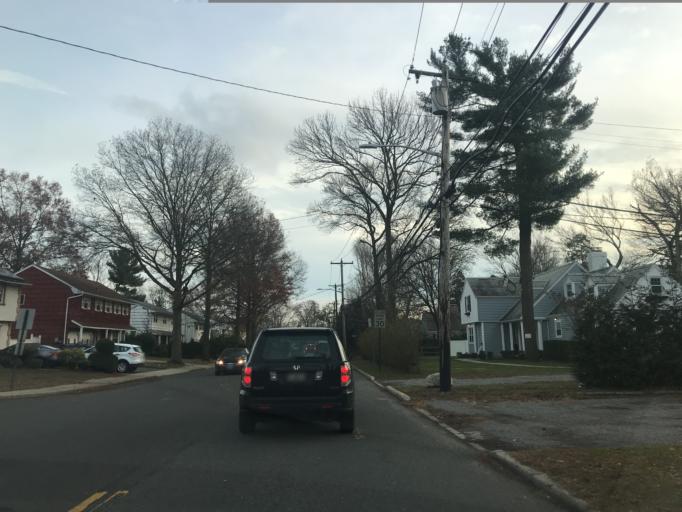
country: US
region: New York
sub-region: Nassau County
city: Carle Place
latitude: 40.7627
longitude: -73.6024
